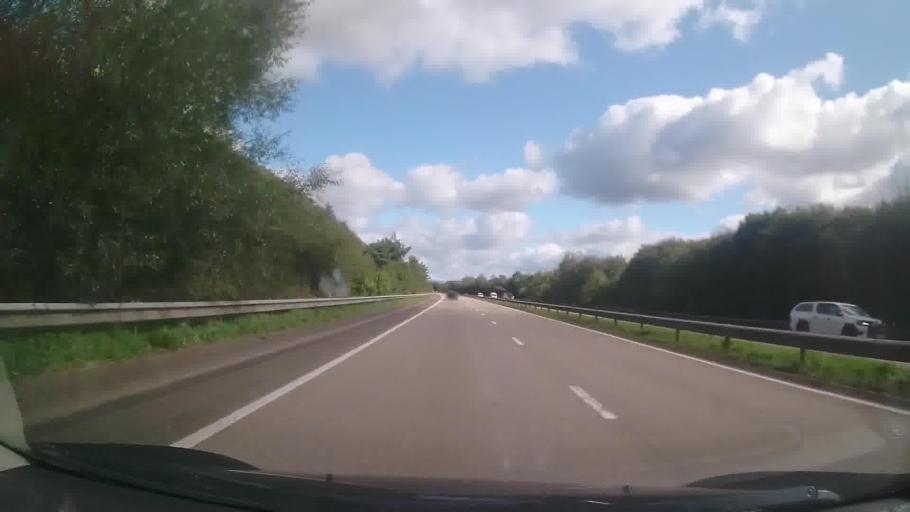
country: GB
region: Wales
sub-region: Neath Port Talbot
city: Crynant
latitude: 51.6893
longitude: -3.7450
